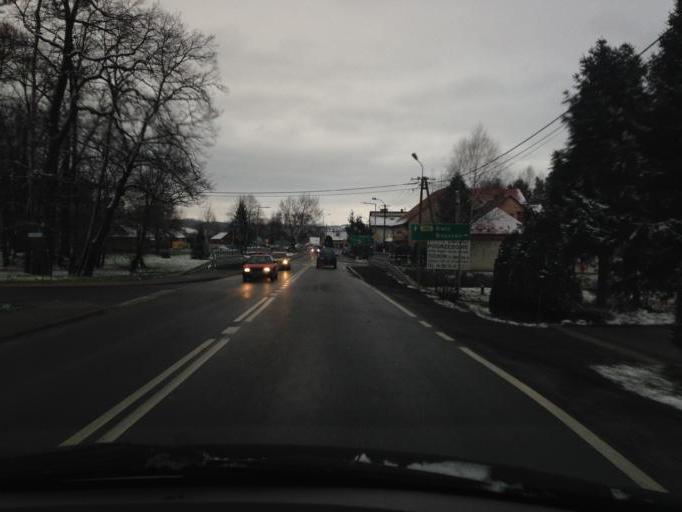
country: PL
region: Lesser Poland Voivodeship
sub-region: Powiat tarnowski
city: Gromnik
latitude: 49.8387
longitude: 20.9581
